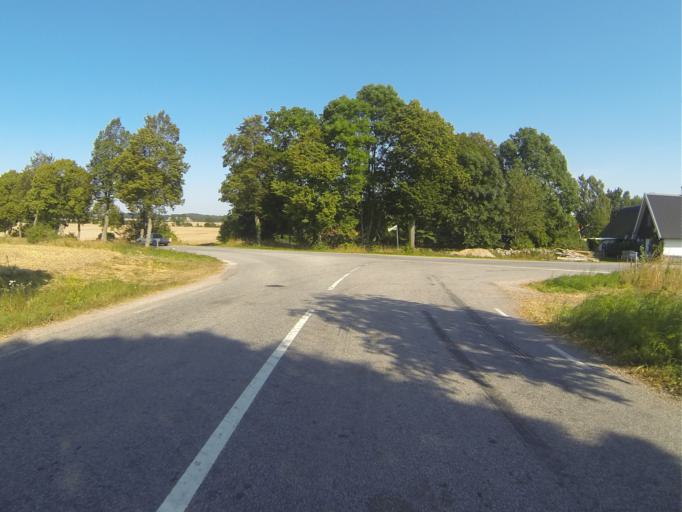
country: SE
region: Skane
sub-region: Sjobo Kommun
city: Sjoebo
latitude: 55.6925
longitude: 13.6452
